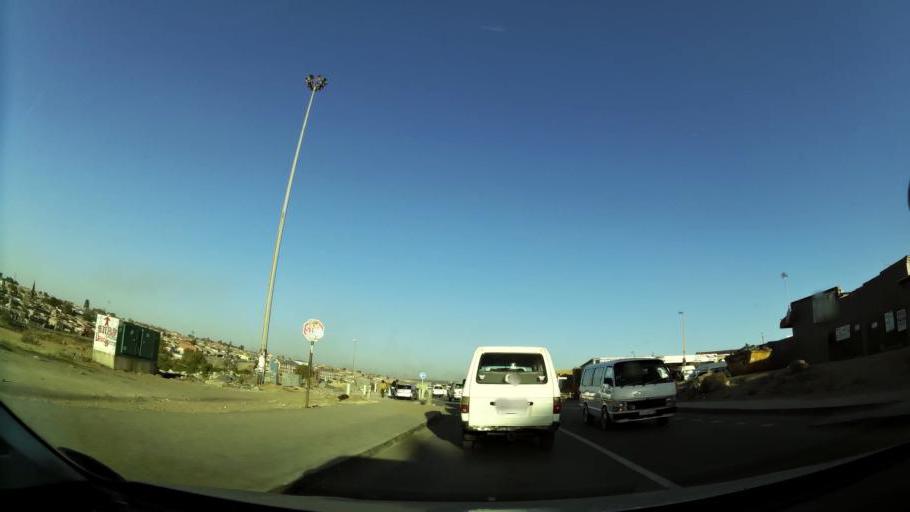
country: ZA
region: Gauteng
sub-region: Ekurhuleni Metropolitan Municipality
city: Tembisa
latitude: -26.0244
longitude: 28.2041
